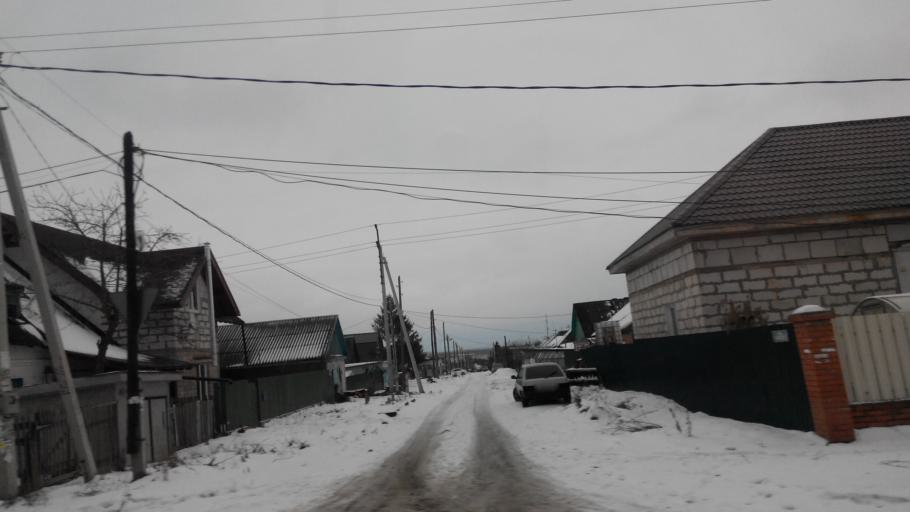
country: RU
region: Tula
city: Uzlovaya
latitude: 53.9819
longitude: 38.1910
